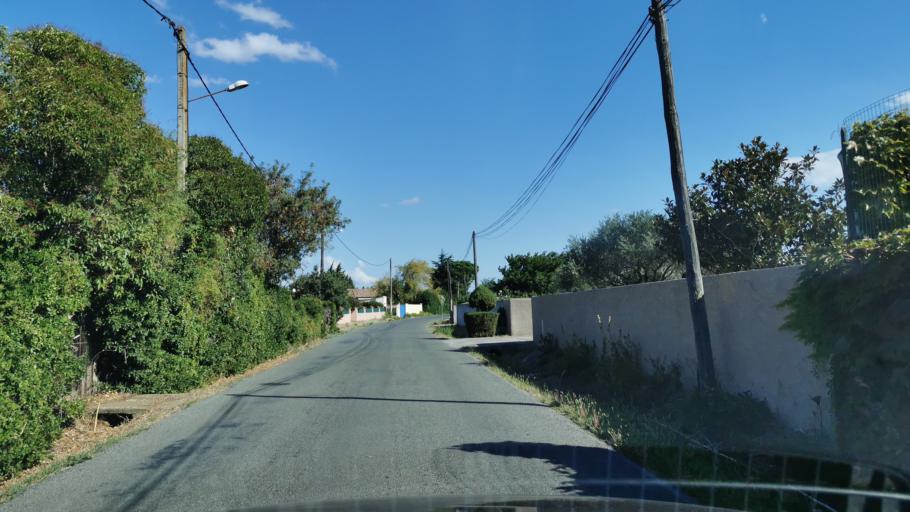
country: FR
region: Languedoc-Roussillon
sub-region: Departement de l'Aude
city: Ginestas
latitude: 43.2472
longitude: 2.8945
